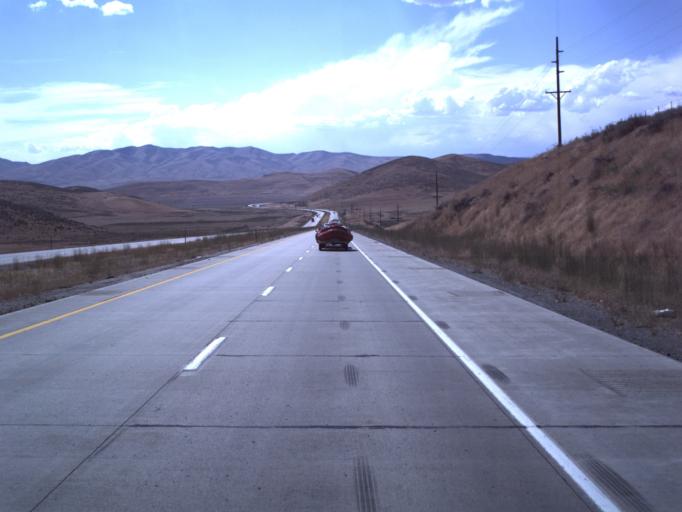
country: US
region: Utah
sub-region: Box Elder County
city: Garland
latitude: 41.8159
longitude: -112.3671
